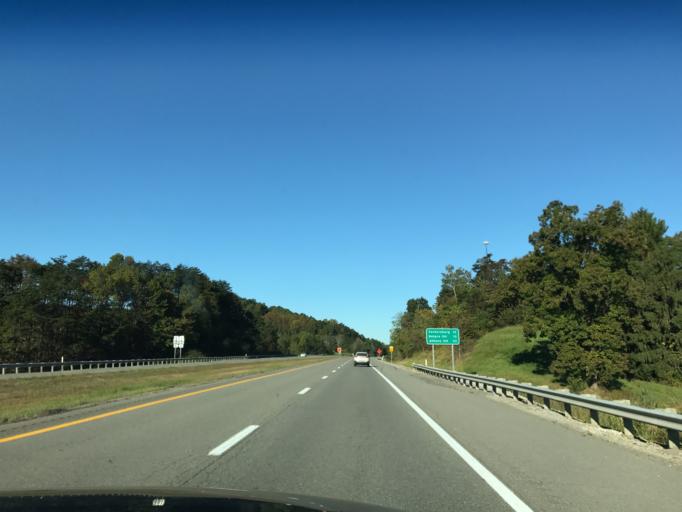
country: US
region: Ohio
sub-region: Washington County
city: Reno
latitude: 39.2516
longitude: -81.3297
